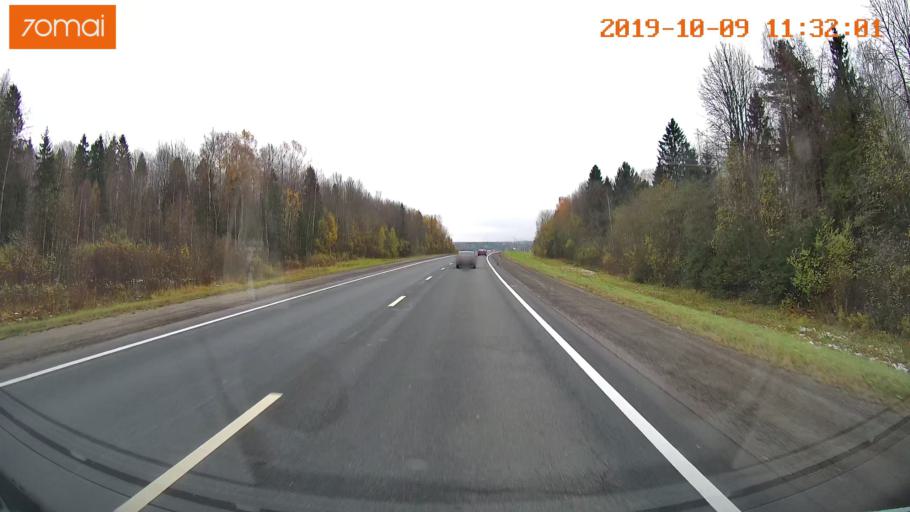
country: RU
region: Vologda
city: Gryazovets
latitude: 59.0401
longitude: 40.1048
